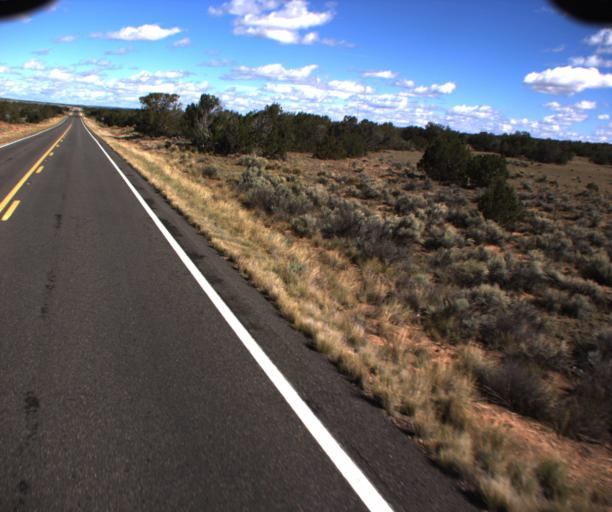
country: US
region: Arizona
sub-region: Apache County
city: Saint Johns
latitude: 34.8837
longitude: -109.2379
